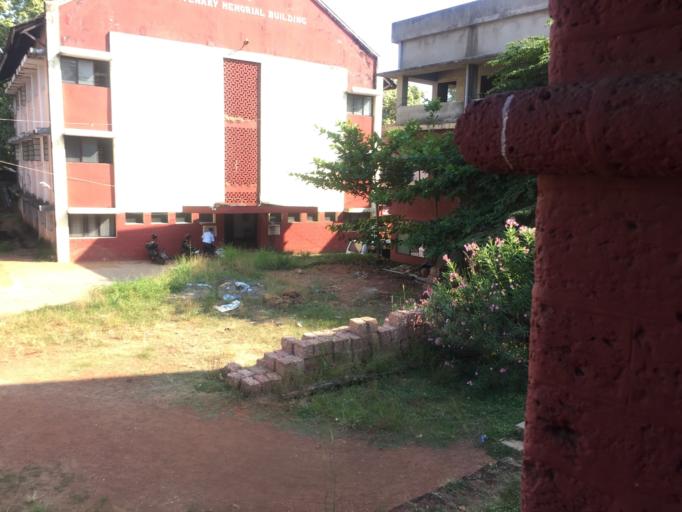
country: IN
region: Karnataka
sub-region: Dakshina Kannada
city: Mangalore
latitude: 12.8656
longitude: 74.8412
